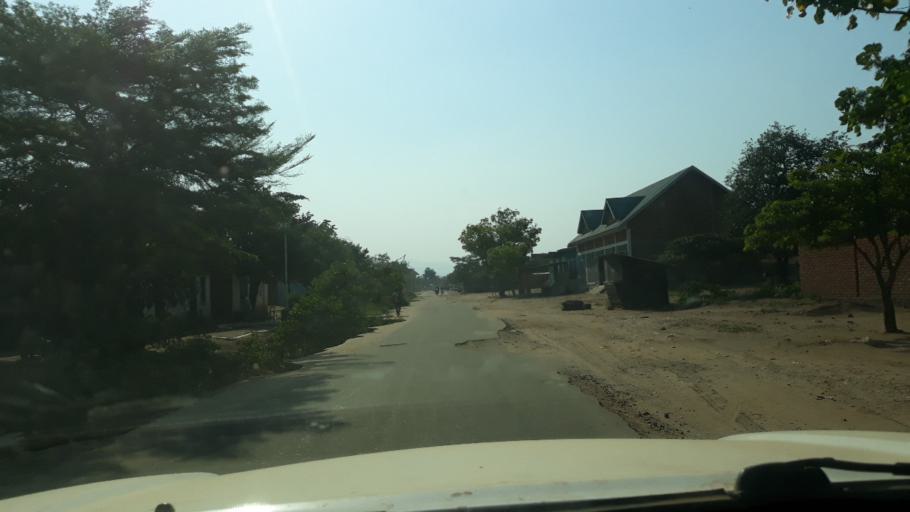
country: BI
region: Cibitoke
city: Cibitoke
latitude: -2.8614
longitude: 29.0318
